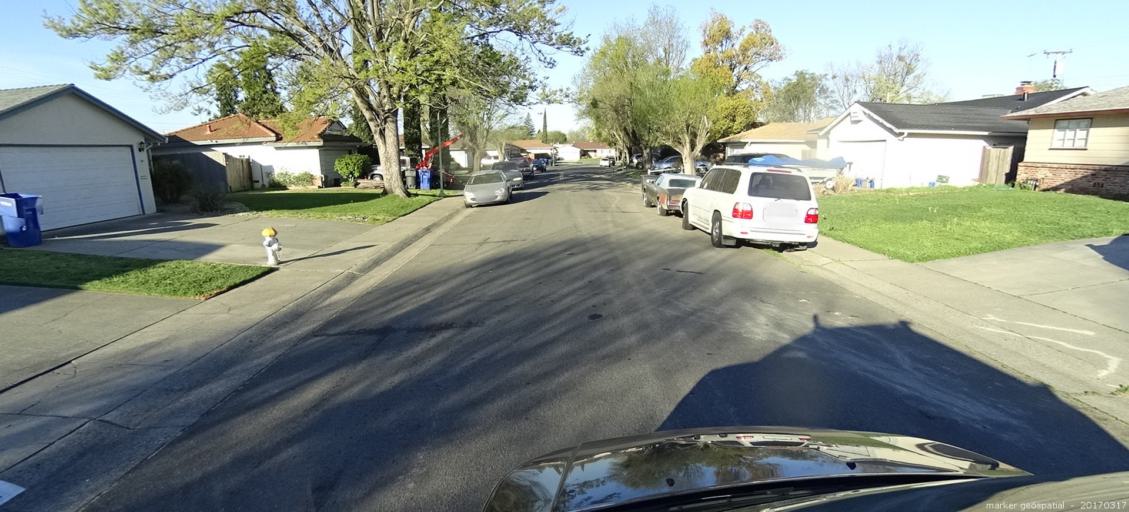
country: US
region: California
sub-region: Sacramento County
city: Parkway
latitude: 38.4936
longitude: -121.4967
